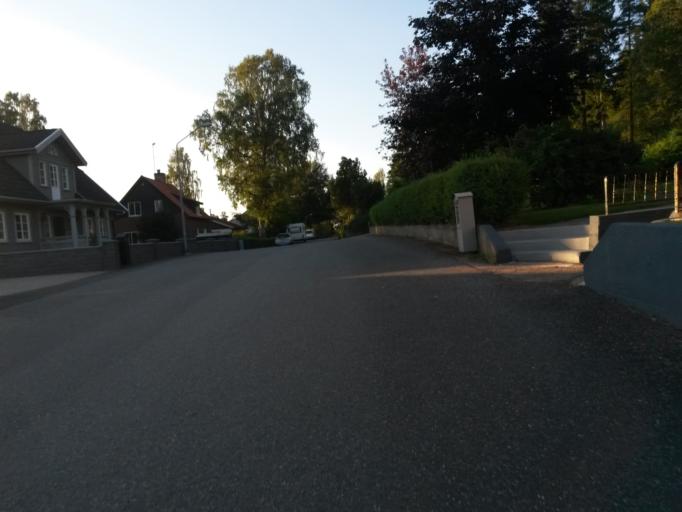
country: SE
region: Vaestra Goetaland
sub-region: Vargarda Kommun
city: Vargarda
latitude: 58.0263
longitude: 12.8012
